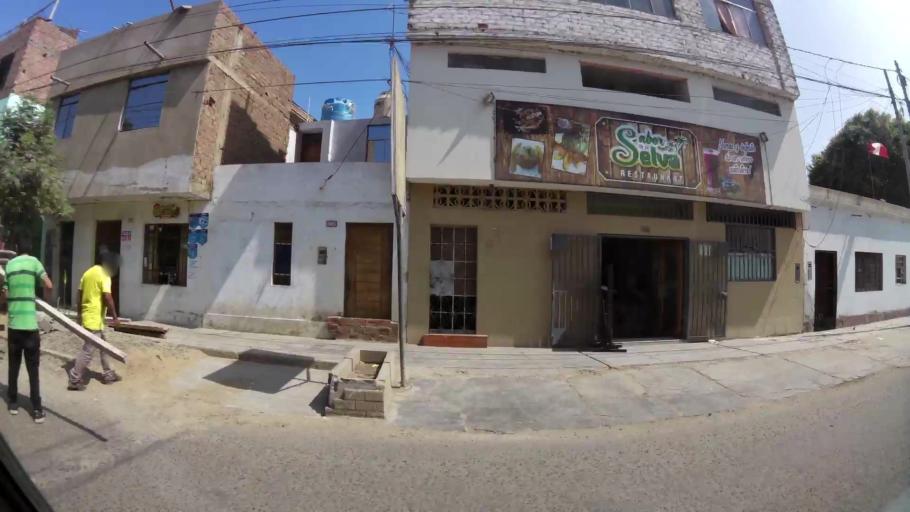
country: PE
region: La Libertad
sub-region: Provincia de Trujillo
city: Buenos Aires
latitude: -8.1345
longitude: -79.0459
